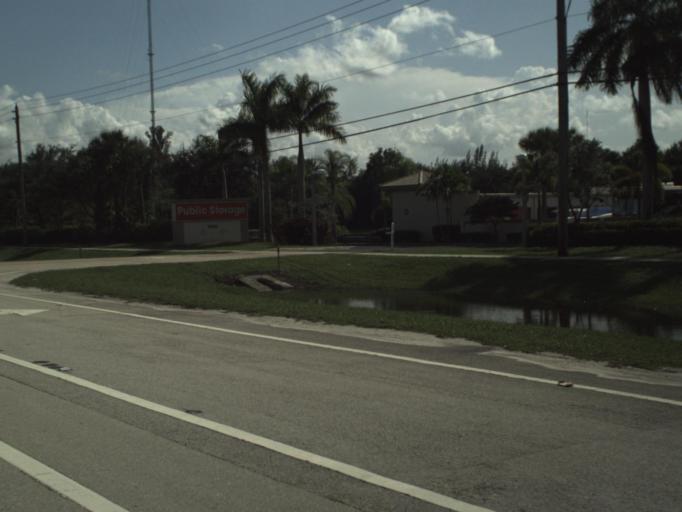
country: US
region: Florida
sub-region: Palm Beach County
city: Wellington
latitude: 26.6004
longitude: -80.2057
